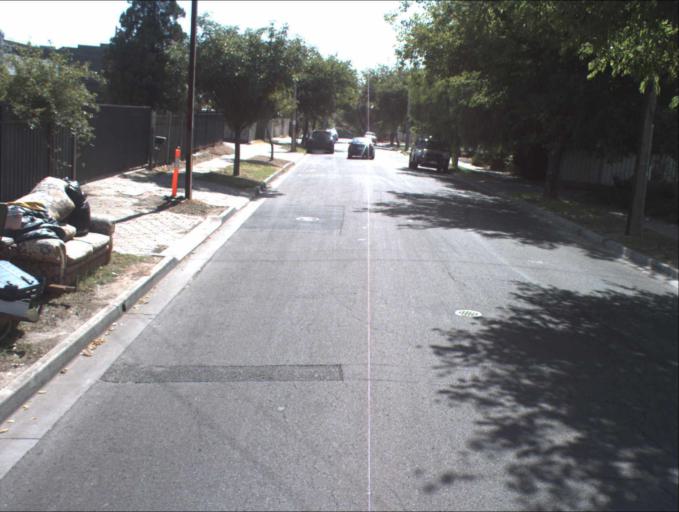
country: AU
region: South Australia
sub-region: Port Adelaide Enfield
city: Gilles Plains
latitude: -34.8652
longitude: 138.6505
